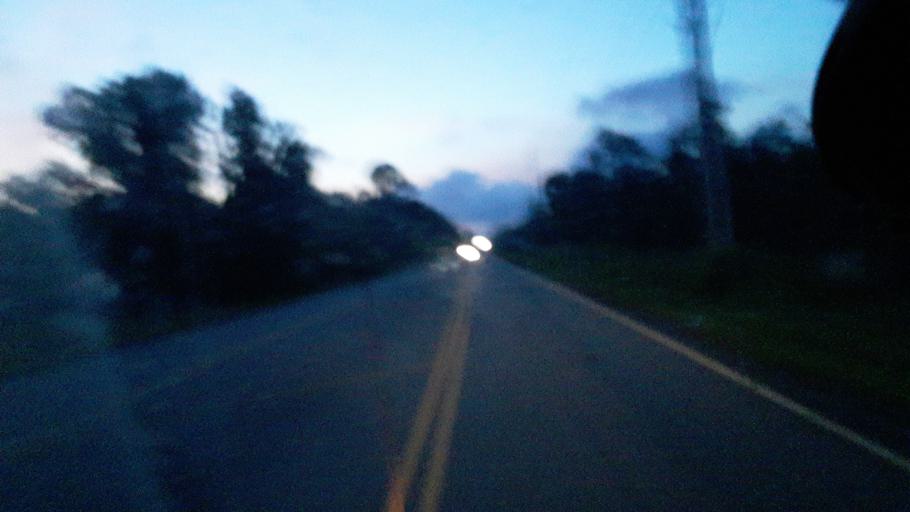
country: US
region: North Carolina
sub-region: Brunswick County
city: Oak Island
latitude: 33.9966
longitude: -78.2336
